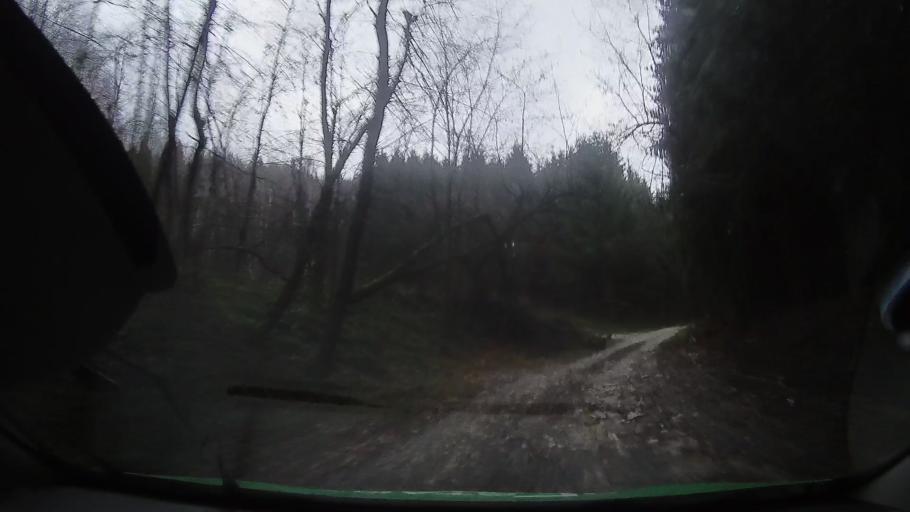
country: RO
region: Alba
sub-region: Comuna Avram Iancu
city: Avram Iancu
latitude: 46.3149
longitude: 22.7890
